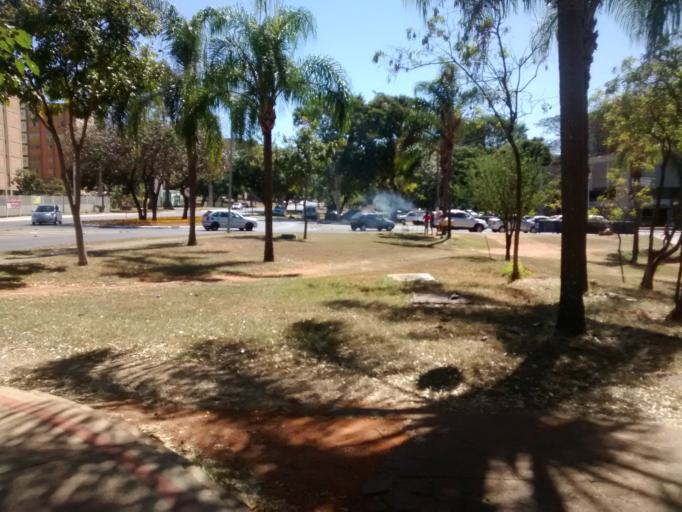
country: BR
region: Federal District
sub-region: Brasilia
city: Brasilia
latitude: -15.7535
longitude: -47.8906
